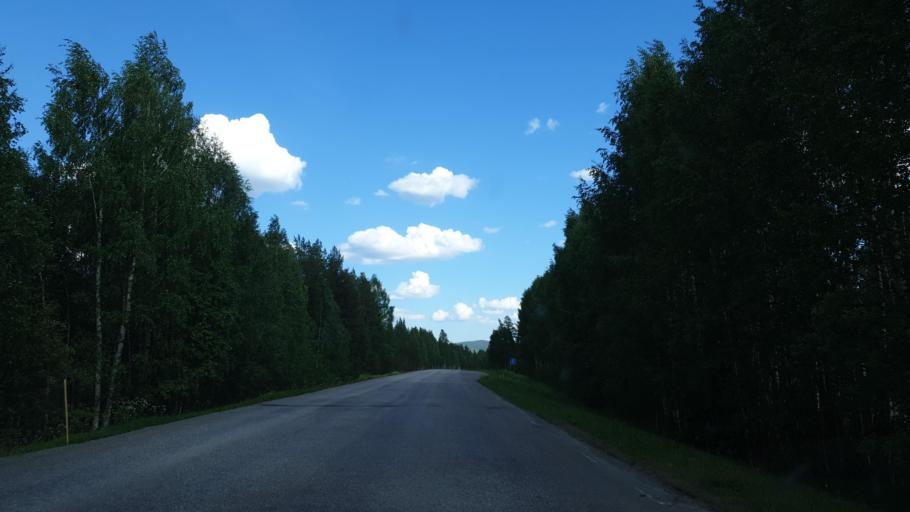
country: SE
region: Norrbotten
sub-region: Alvsbyns Kommun
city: AElvsbyn
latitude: 65.8450
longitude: 20.4841
